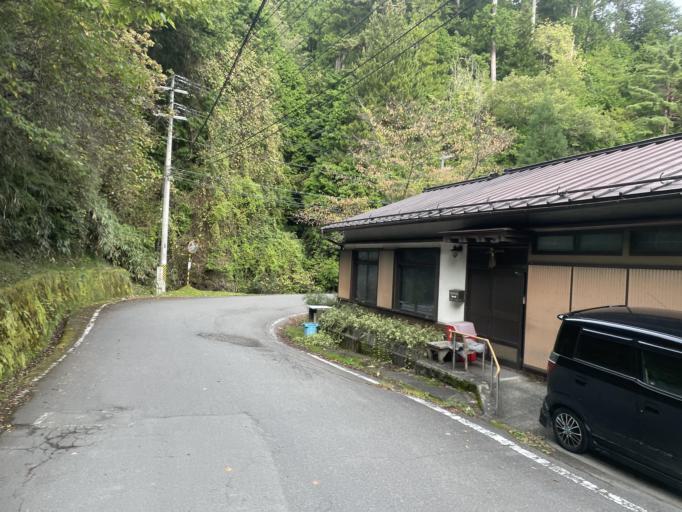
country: JP
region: Wakayama
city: Koya
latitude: 34.2267
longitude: 135.5763
